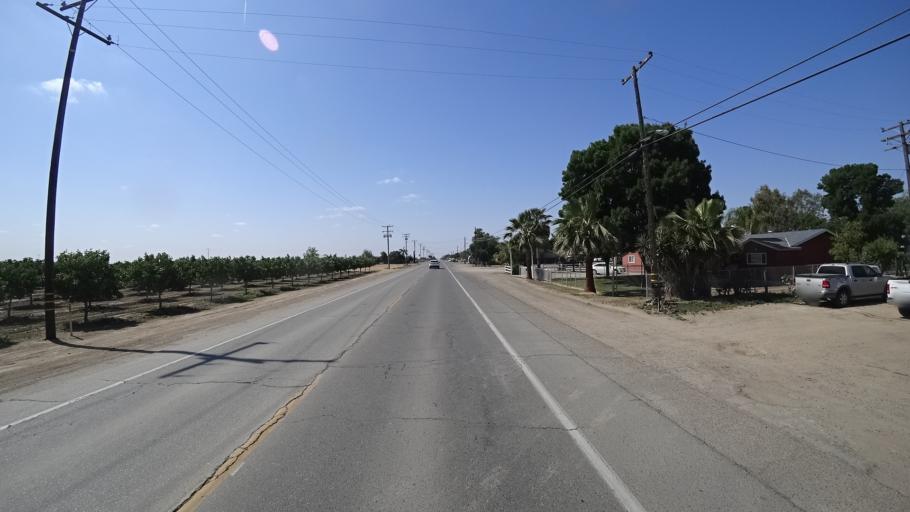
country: US
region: California
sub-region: Kings County
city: Home Garden
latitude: 36.2924
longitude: -119.6369
